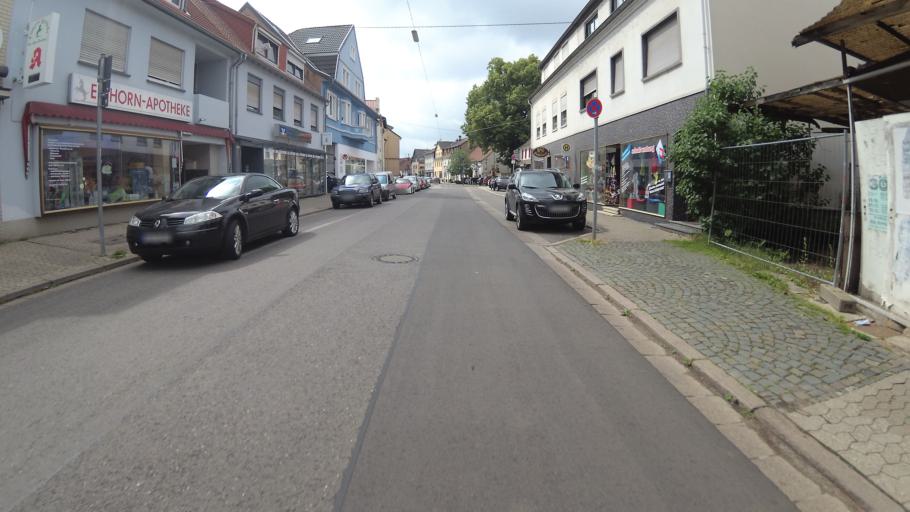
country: FR
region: Lorraine
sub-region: Departement de la Moselle
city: Alsting
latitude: 49.2005
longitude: 7.0280
